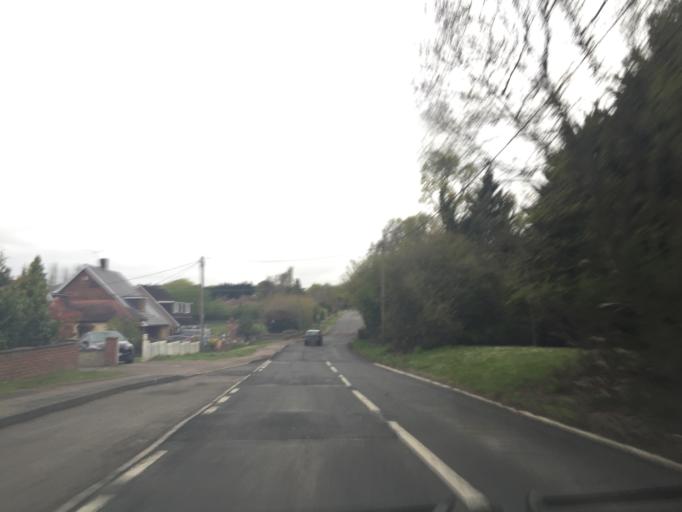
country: GB
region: England
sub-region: Greater London
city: Collier Row
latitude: 51.6317
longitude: 0.1747
